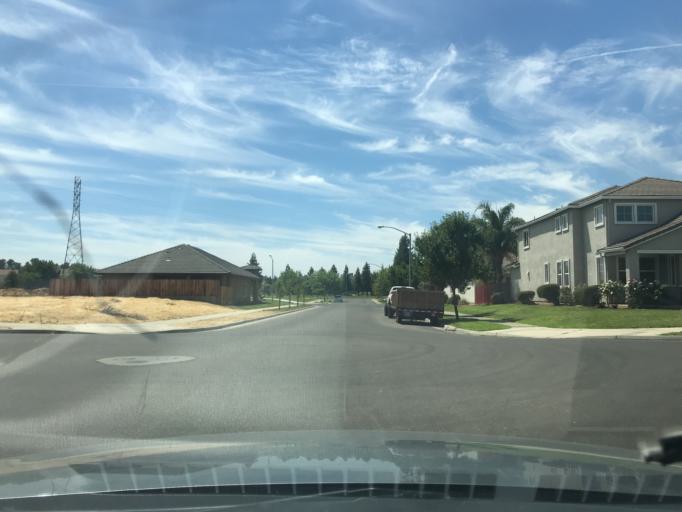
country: US
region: California
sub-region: Merced County
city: Merced
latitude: 37.3383
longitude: -120.4932
